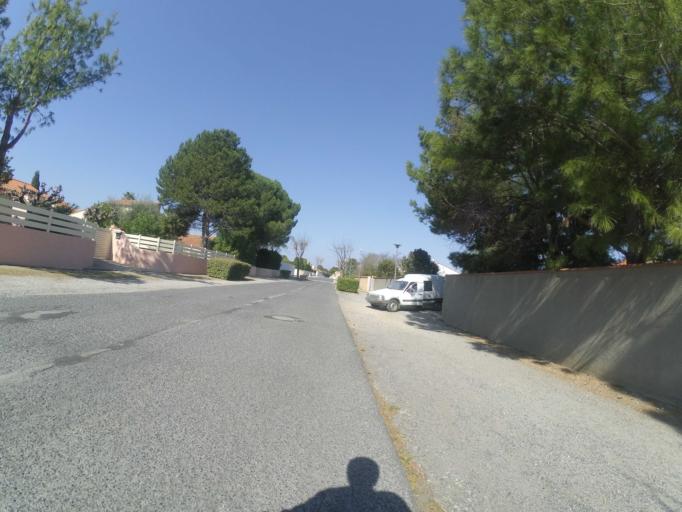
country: FR
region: Languedoc-Roussillon
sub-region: Departement des Pyrenees-Orientales
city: Llupia
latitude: 42.6230
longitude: 2.7659
